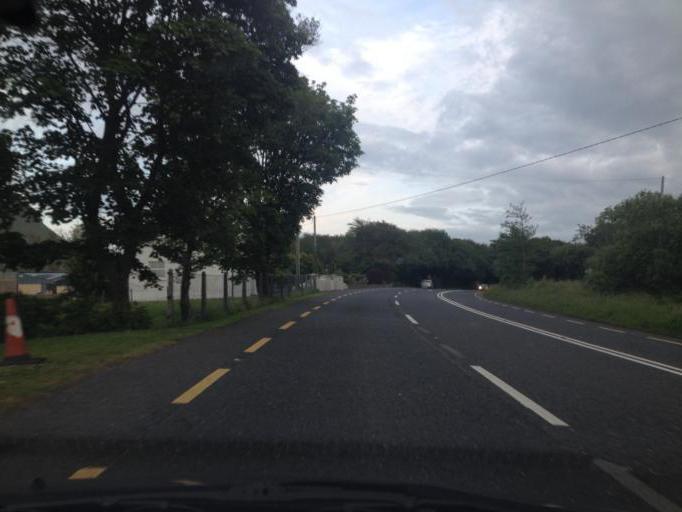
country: IE
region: Connaught
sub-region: Sligo
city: Strandhill
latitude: 54.3835
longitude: -8.5295
